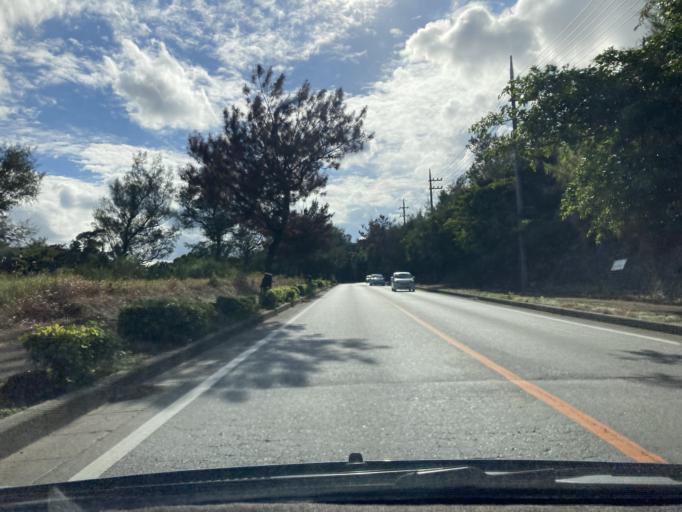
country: JP
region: Okinawa
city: Ishikawa
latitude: 26.4333
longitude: 127.8074
